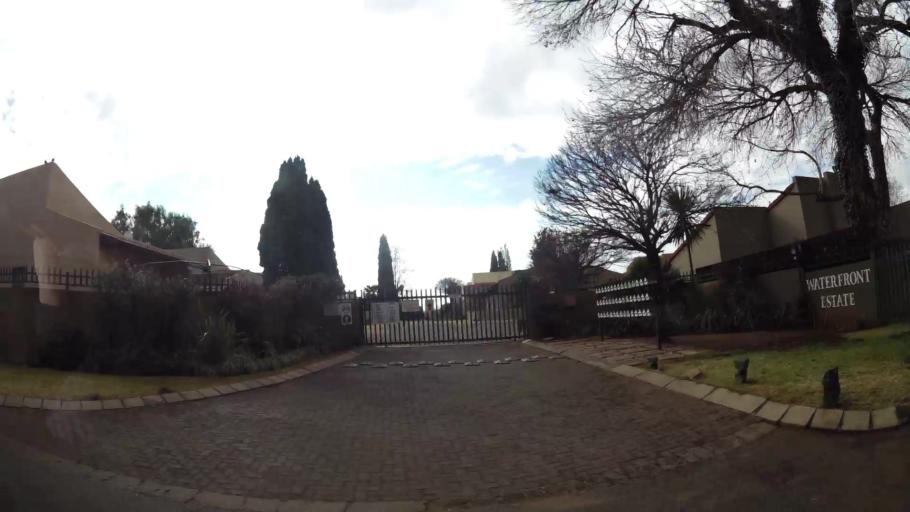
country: ZA
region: Gauteng
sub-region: Sedibeng District Municipality
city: Meyerton
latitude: -26.5897
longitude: 28.0156
